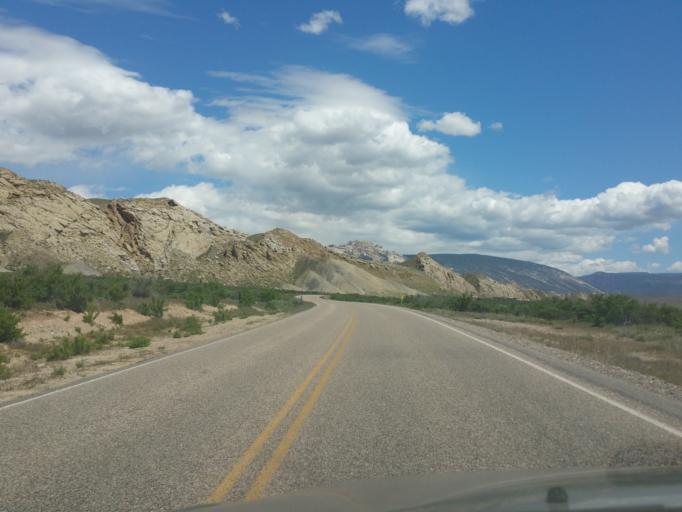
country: US
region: Utah
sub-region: Uintah County
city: Naples
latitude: 40.4380
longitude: -109.3198
